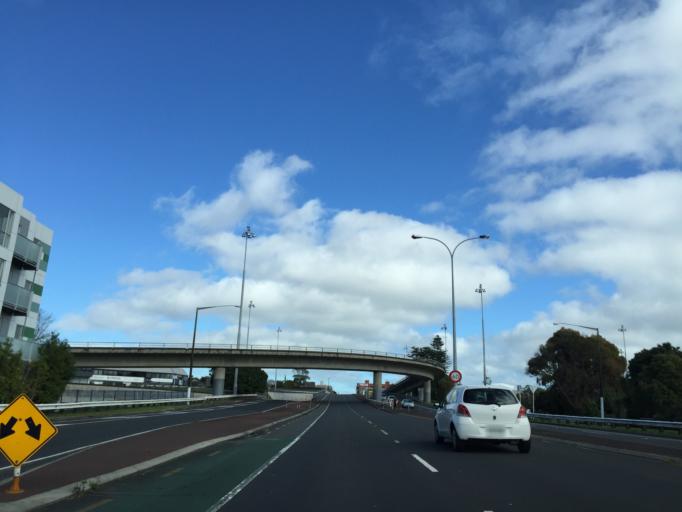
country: NZ
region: Auckland
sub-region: Auckland
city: Auckland
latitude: -36.8669
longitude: 174.7542
